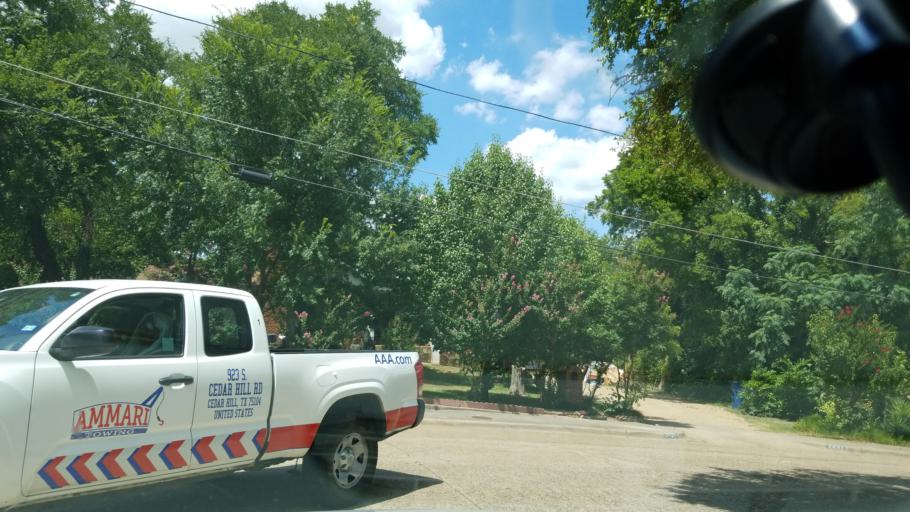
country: US
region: Texas
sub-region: Dallas County
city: Cockrell Hill
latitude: 32.6970
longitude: -96.8584
